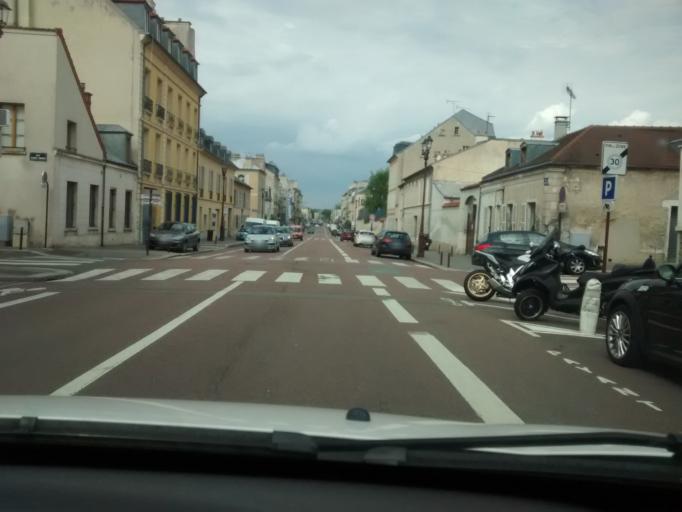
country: FR
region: Ile-de-France
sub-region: Departement des Yvelines
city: Versailles
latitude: 48.7938
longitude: 2.1242
